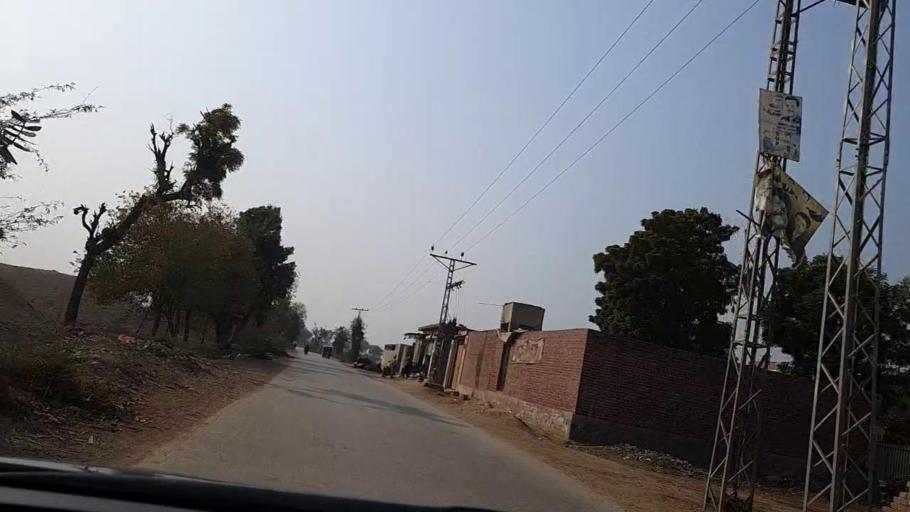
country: PK
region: Sindh
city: Sakrand
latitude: 26.1369
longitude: 68.2443
